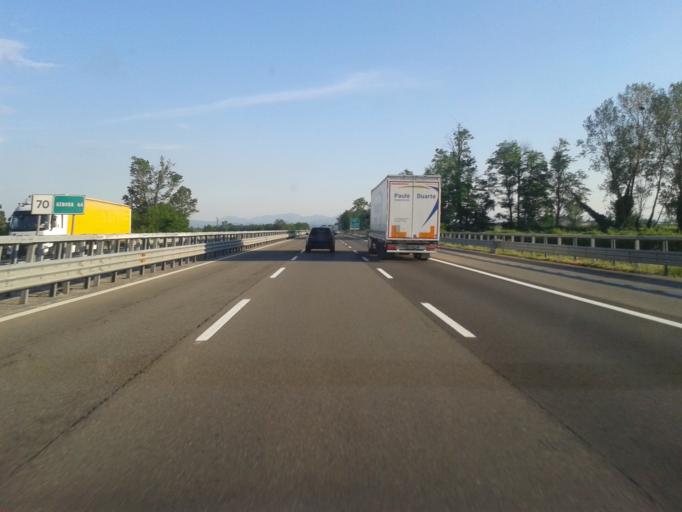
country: IT
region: Piedmont
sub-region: Provincia di Alessandria
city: Carbonara Scrivia
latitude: 44.8529
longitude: 8.8294
